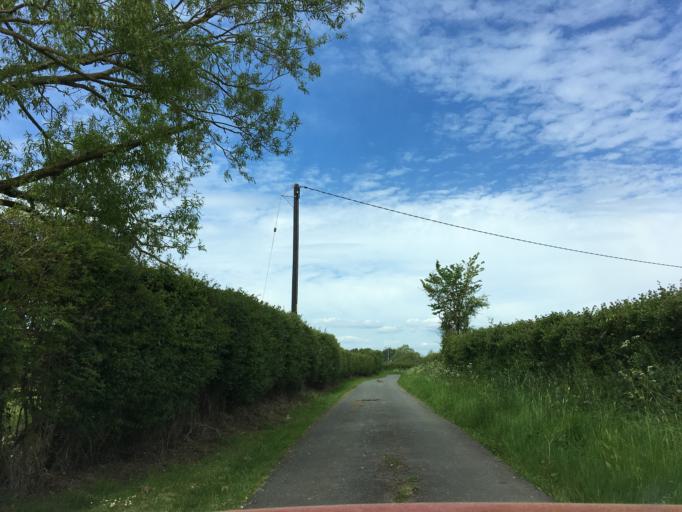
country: GB
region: England
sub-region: South Gloucestershire
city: Charfield
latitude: 51.6681
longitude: -2.4057
